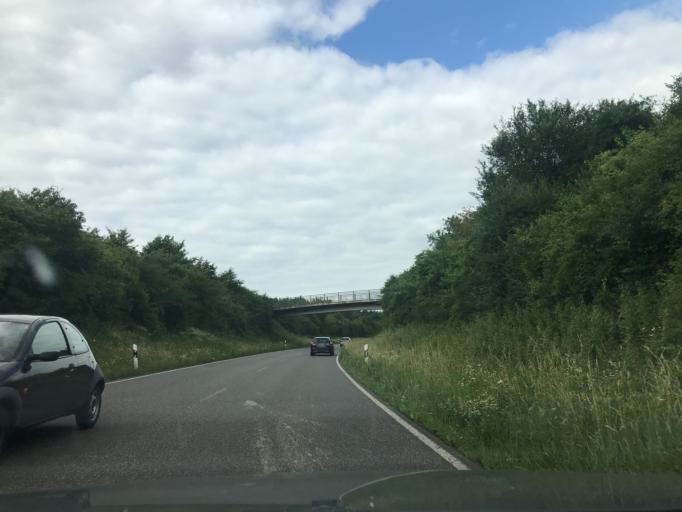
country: DE
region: North Rhine-Westphalia
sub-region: Regierungsbezirk Dusseldorf
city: Neuss
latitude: 51.1570
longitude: 6.7166
